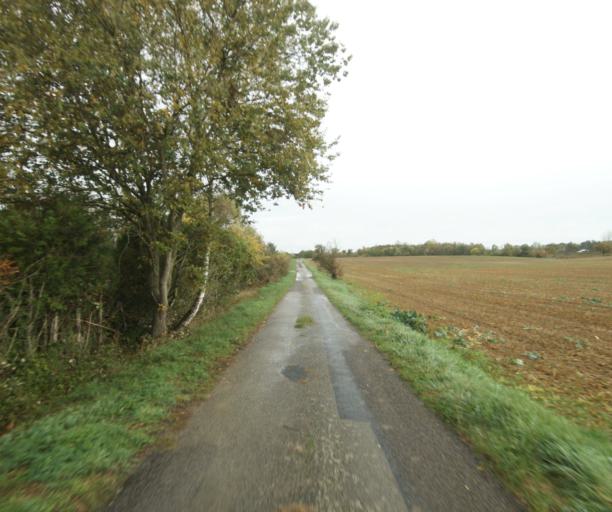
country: FR
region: Rhone-Alpes
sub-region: Departement de l'Ain
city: Pont-de-Vaux
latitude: 46.4835
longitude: 4.8880
